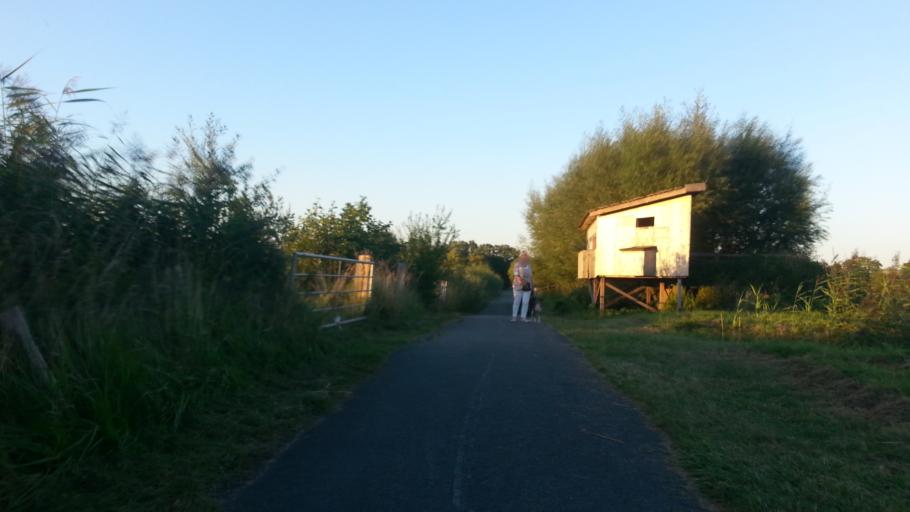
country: DE
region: North Rhine-Westphalia
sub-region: Regierungsbezirk Munster
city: Muenster
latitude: 52.0233
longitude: 7.6590
